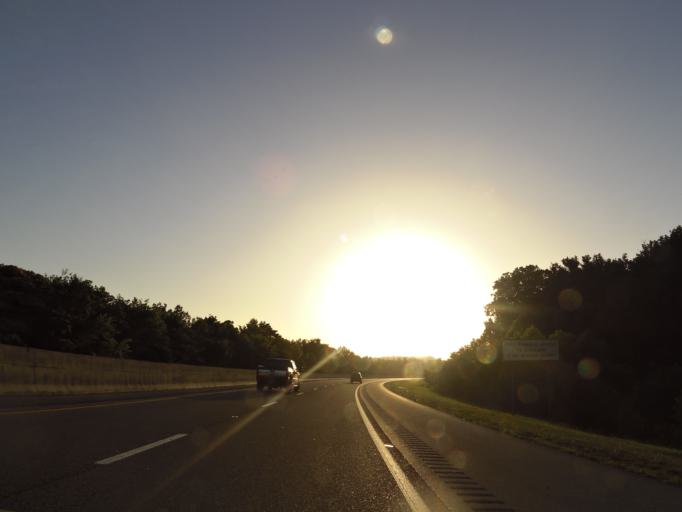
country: US
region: Tennessee
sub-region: Blount County
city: Louisville
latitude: 35.8501
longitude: -84.0159
